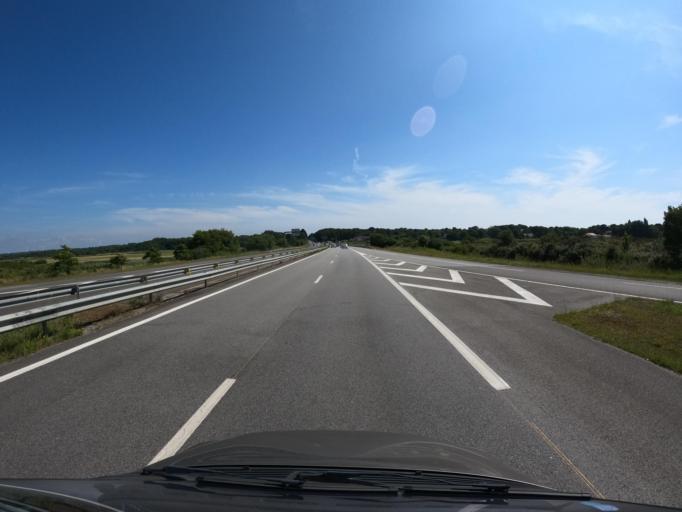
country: FR
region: Pays de la Loire
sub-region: Departement de la Loire-Atlantique
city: Saint-Michel-Chef-Chef
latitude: 47.2131
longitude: -2.1512
